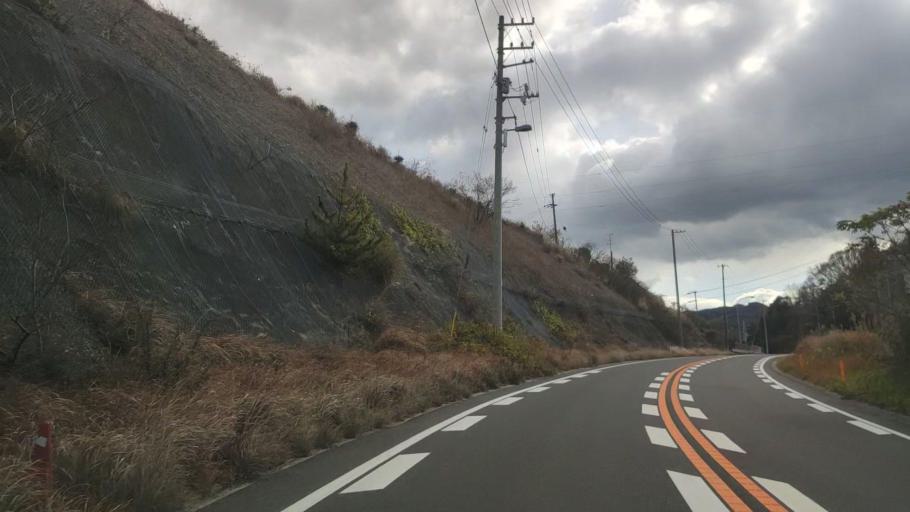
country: JP
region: Ehime
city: Hojo
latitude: 34.0622
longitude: 132.9144
